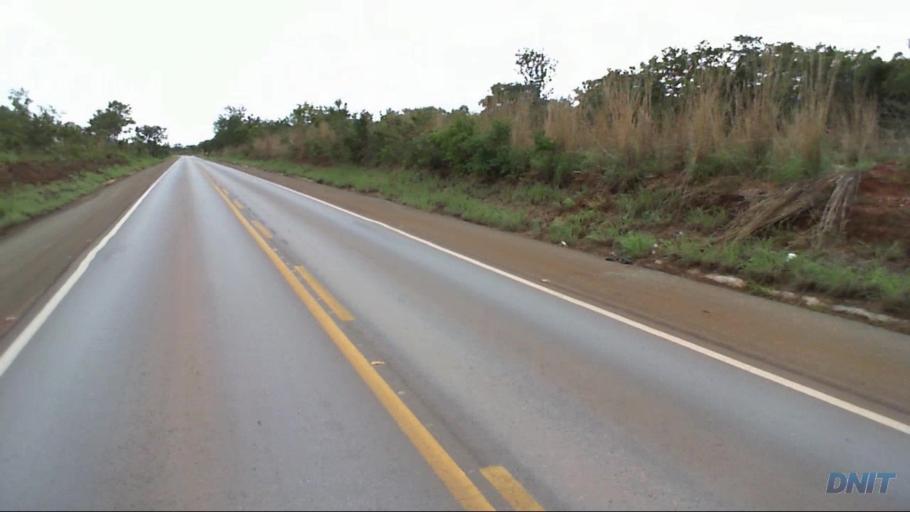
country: BR
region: Goias
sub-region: Barro Alto
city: Barro Alto
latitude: -14.7866
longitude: -49.0541
